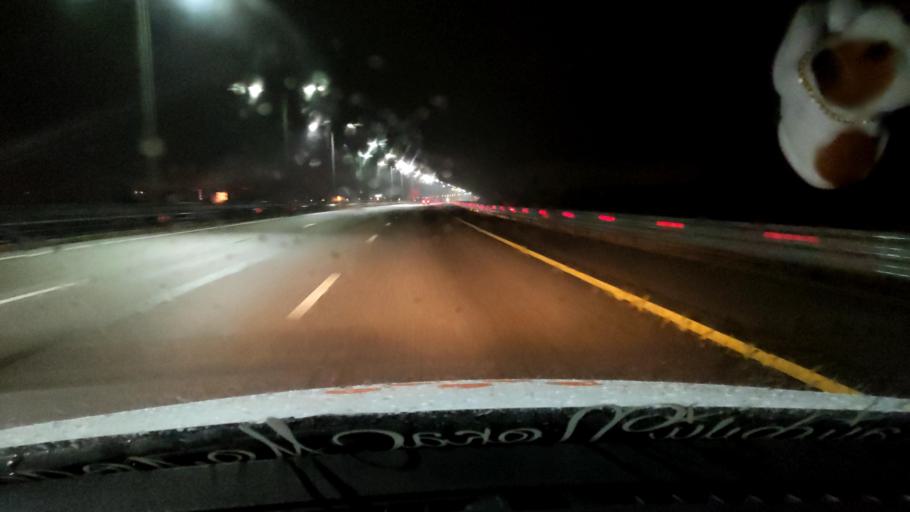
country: RU
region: Voronezj
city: Somovo
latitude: 51.7594
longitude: 39.3068
